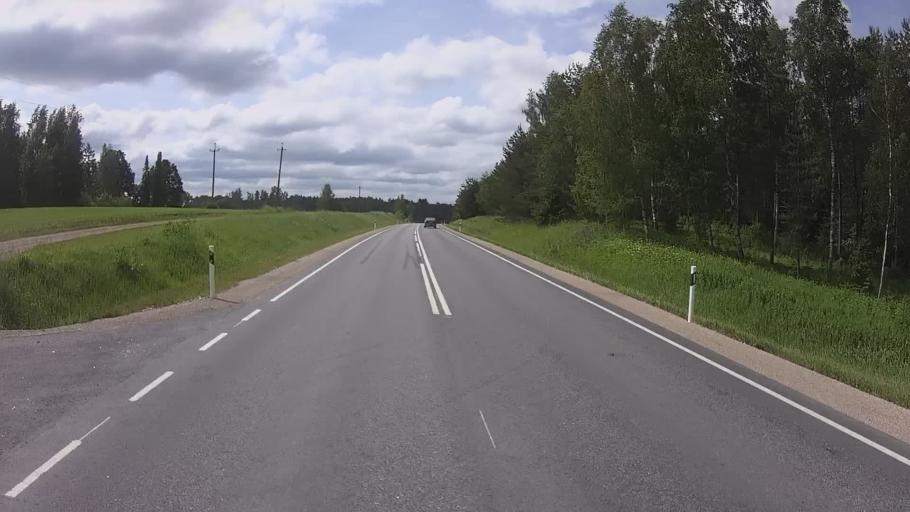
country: EE
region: Polvamaa
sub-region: Polva linn
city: Polva
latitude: 58.0501
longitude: 27.0763
